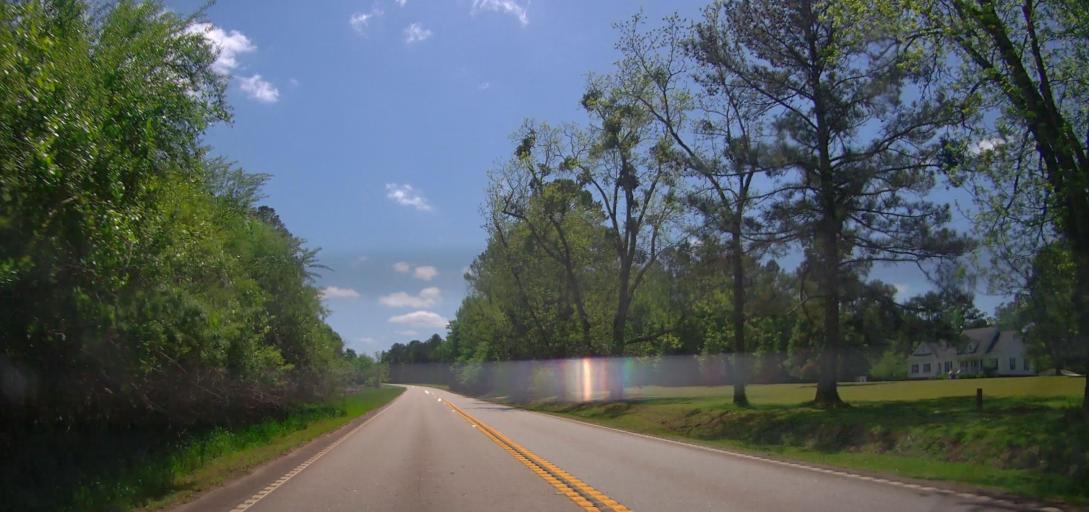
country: US
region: Georgia
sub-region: Jasper County
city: Monticello
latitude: 33.2272
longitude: -83.6745
